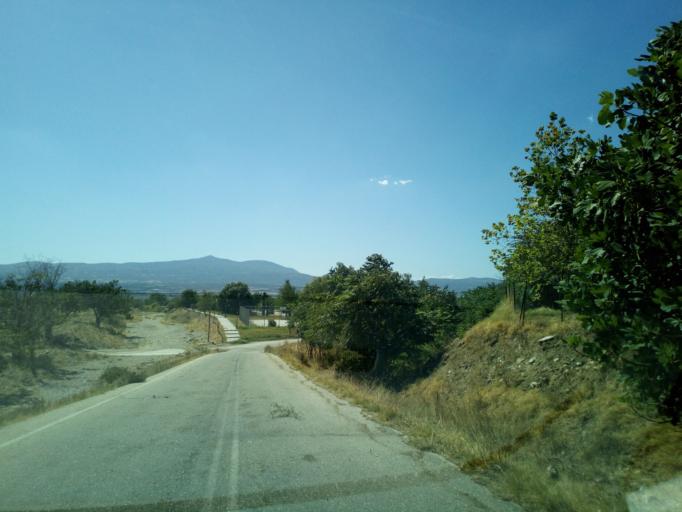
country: GR
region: Central Macedonia
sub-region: Nomos Thessalonikis
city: Gerakarou
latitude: 40.6943
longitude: 23.2220
